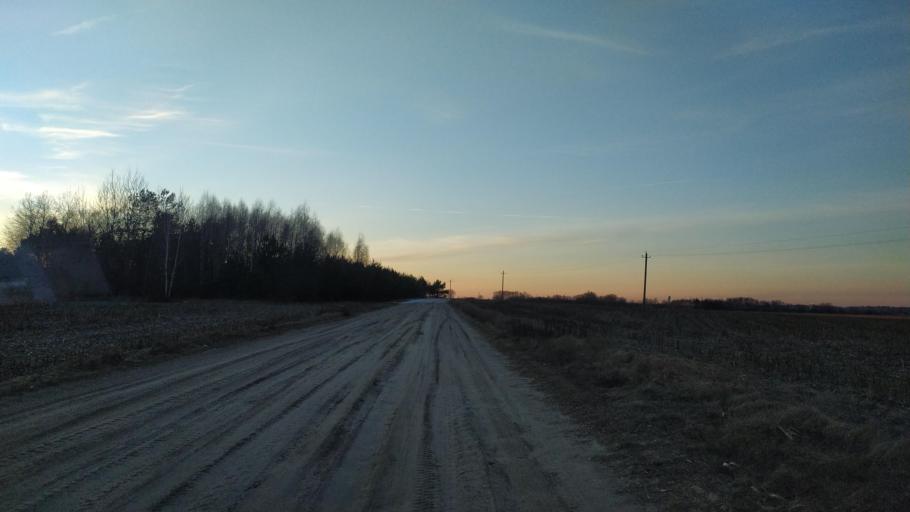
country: BY
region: Brest
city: Pruzhany
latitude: 52.5470
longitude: 24.2420
